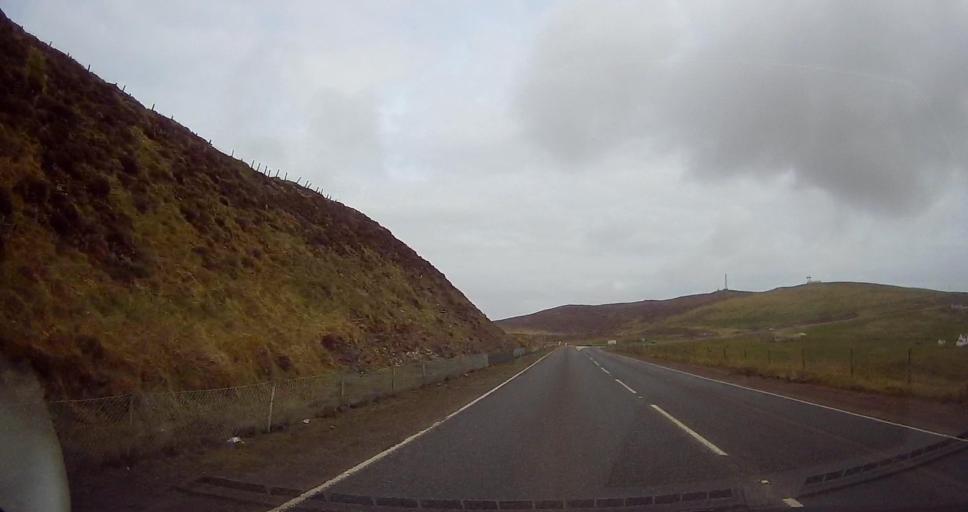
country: GB
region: Scotland
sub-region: Shetland Islands
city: Lerwick
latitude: 60.1344
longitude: -1.2136
